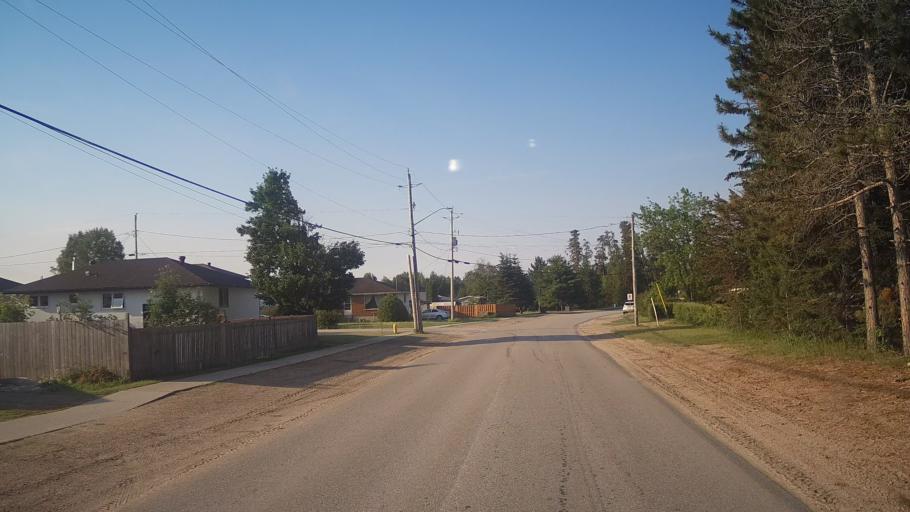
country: CA
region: Ontario
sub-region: Rainy River District
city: Atikokan
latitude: 49.4102
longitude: -91.6574
